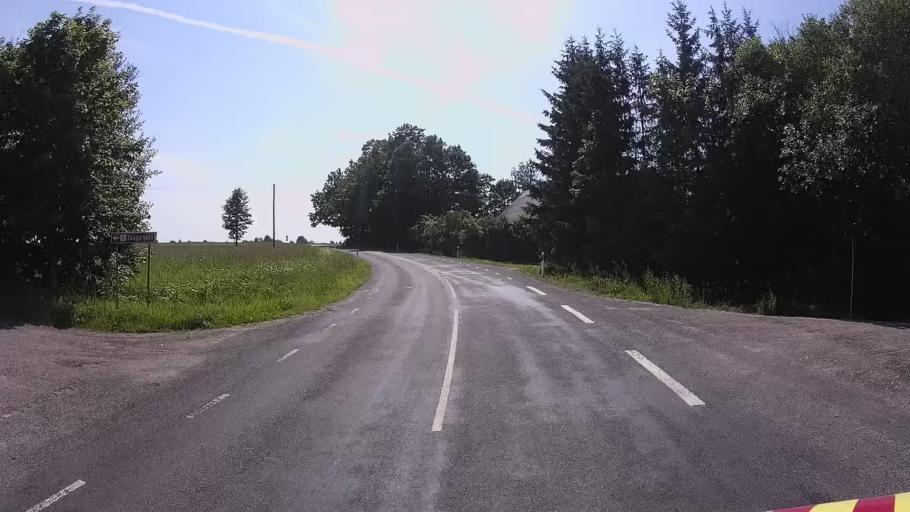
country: EE
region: Viljandimaa
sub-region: Karksi vald
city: Karksi-Nuia
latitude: 58.0723
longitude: 25.5559
